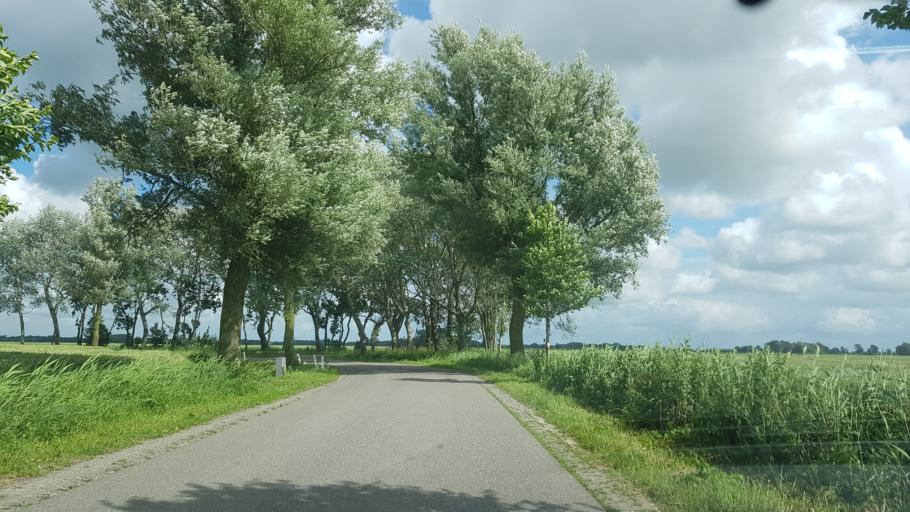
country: NL
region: Groningen
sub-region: Gemeente Winsum
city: Winsum
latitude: 53.3955
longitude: 6.4722
